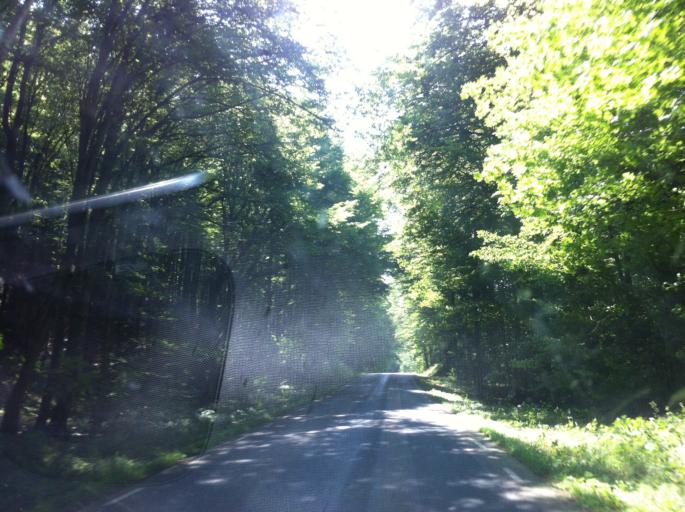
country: SE
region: Skane
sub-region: Hoors Kommun
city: Hoeoer
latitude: 56.0123
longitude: 13.4945
